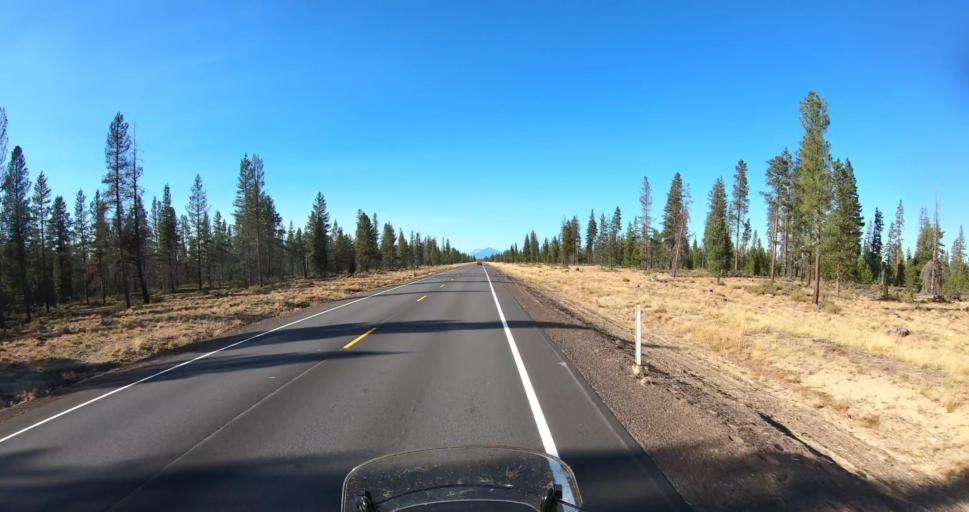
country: US
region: Oregon
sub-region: Deschutes County
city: La Pine
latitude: 43.5798
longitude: -121.4868
